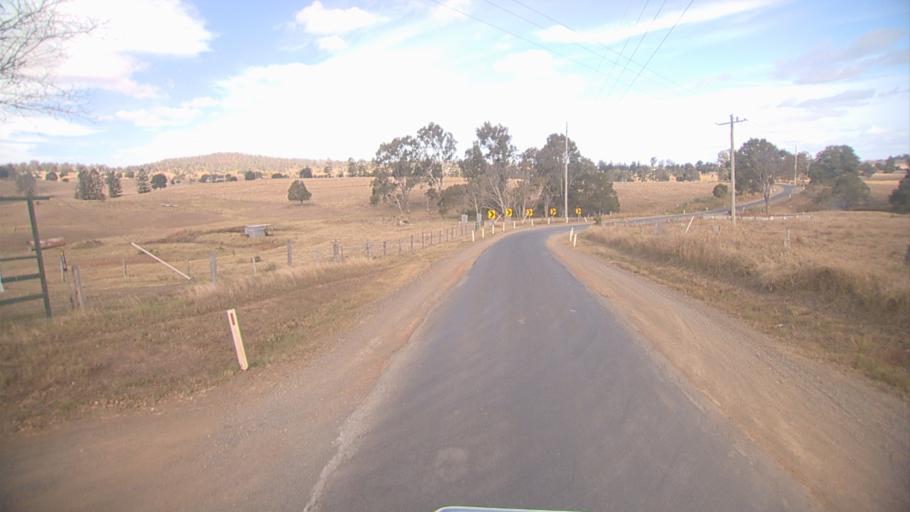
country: AU
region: Queensland
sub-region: Logan
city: Cedar Vale
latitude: -27.9111
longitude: 153.0138
